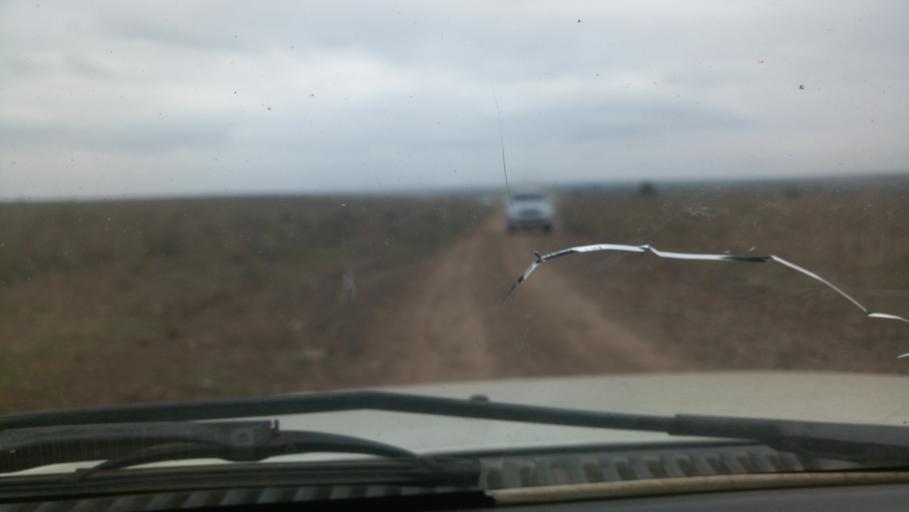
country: KE
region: Nairobi Area
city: Pumwani
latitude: -1.3758
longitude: 36.8647
